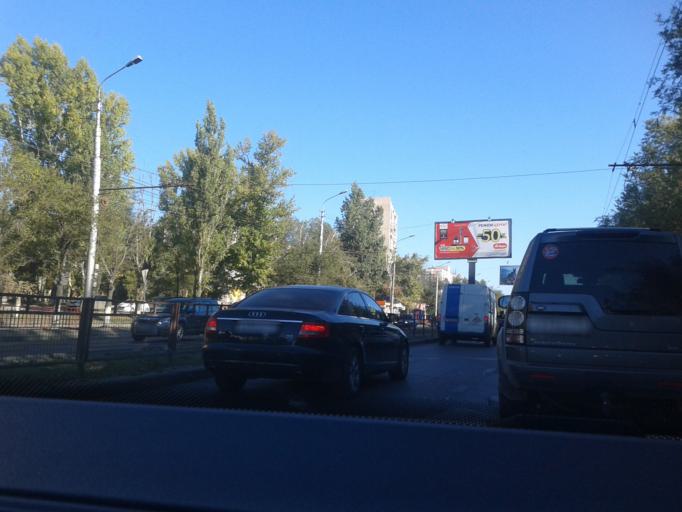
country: RU
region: Volgograd
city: Volgograd
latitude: 48.6196
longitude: 44.4243
